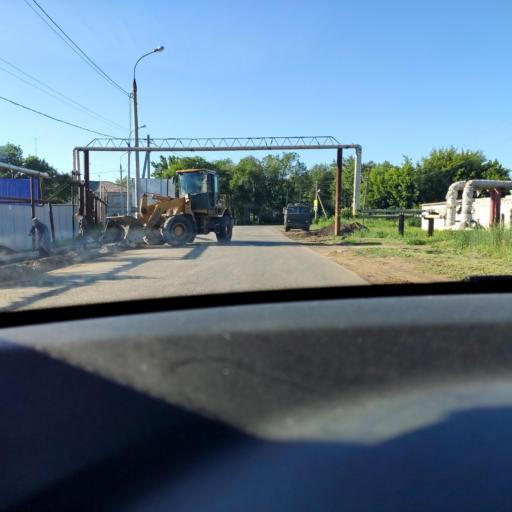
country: RU
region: Samara
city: Samara
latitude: 53.1369
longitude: 50.2357
